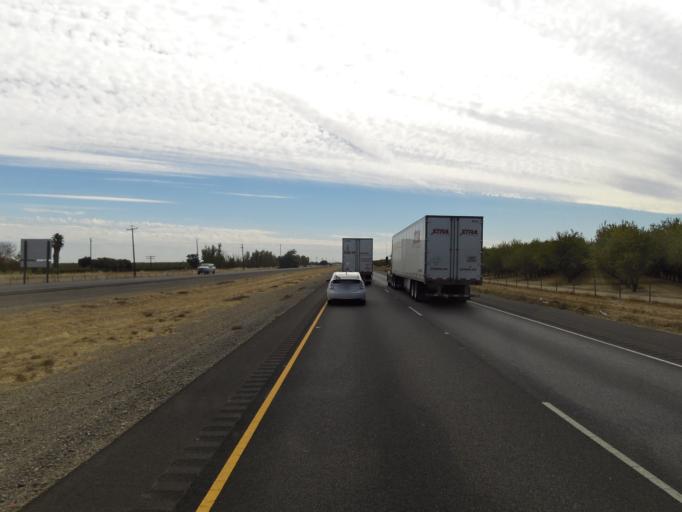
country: US
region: California
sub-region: Colusa County
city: Arbuckle
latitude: 38.9971
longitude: -122.0441
